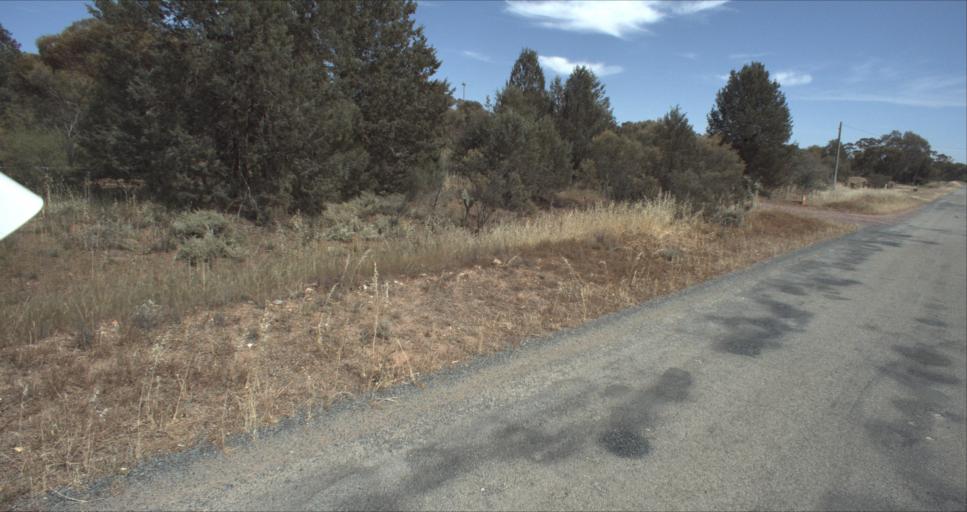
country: AU
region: New South Wales
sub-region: Leeton
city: Leeton
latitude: -34.5672
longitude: 146.4636
